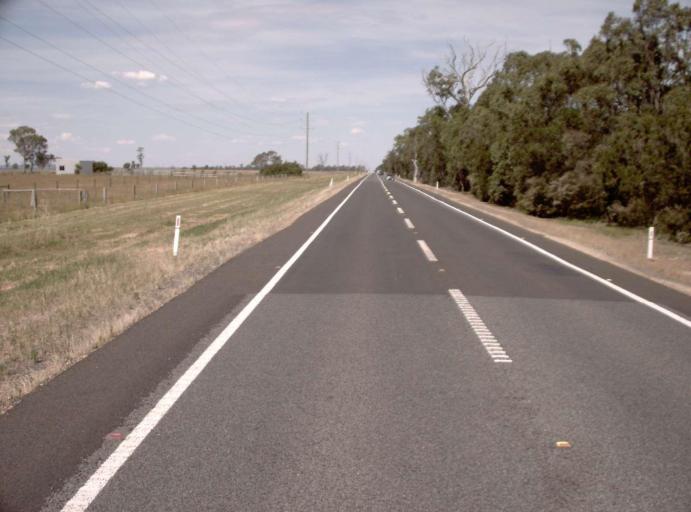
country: AU
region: Victoria
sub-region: East Gippsland
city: Bairnsdale
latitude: -37.8709
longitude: 147.4684
